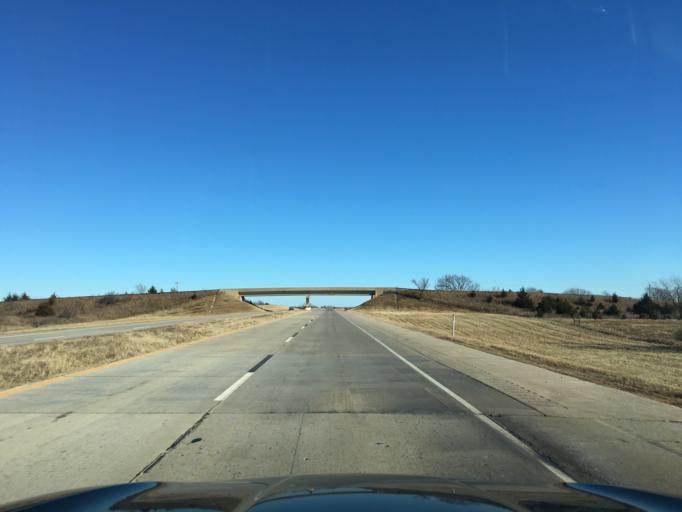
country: US
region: Oklahoma
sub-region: Payne County
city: Yale
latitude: 36.2247
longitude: -96.7153
